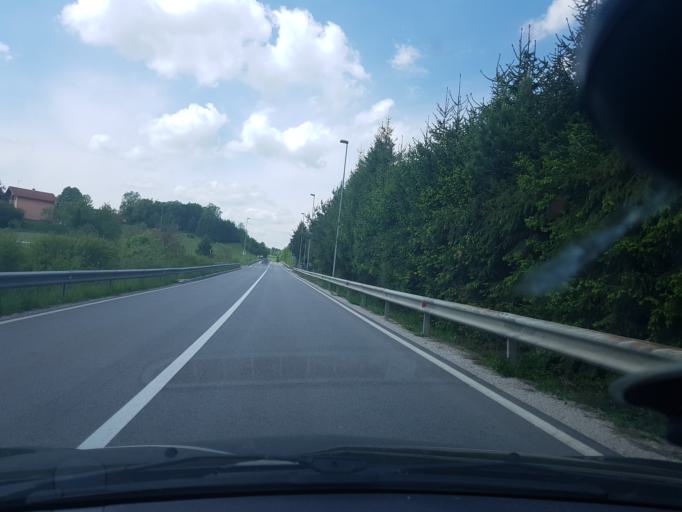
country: SI
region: Rogaska Slatina
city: Rogaska Slatina
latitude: 46.2411
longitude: 15.6679
